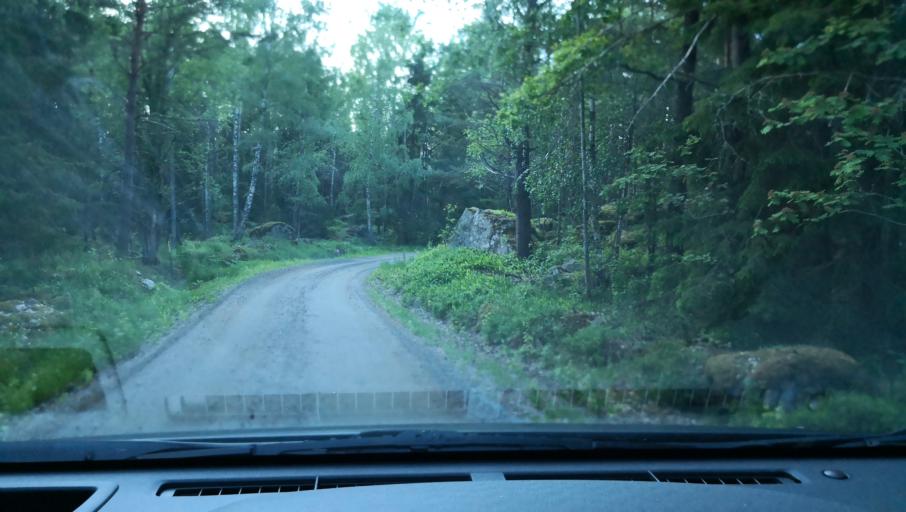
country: SE
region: Uppsala
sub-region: Enkopings Kommun
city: Orsundsbro
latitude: 59.8375
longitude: 17.2197
